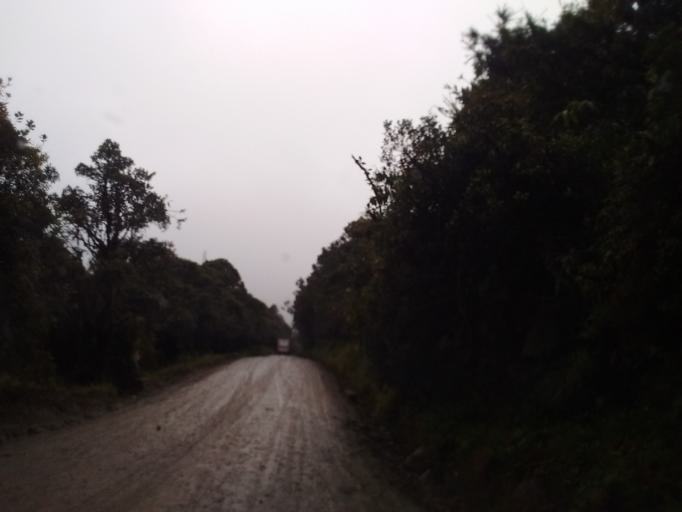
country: CO
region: Cauca
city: Paispamba
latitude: 2.1549
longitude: -76.4513
